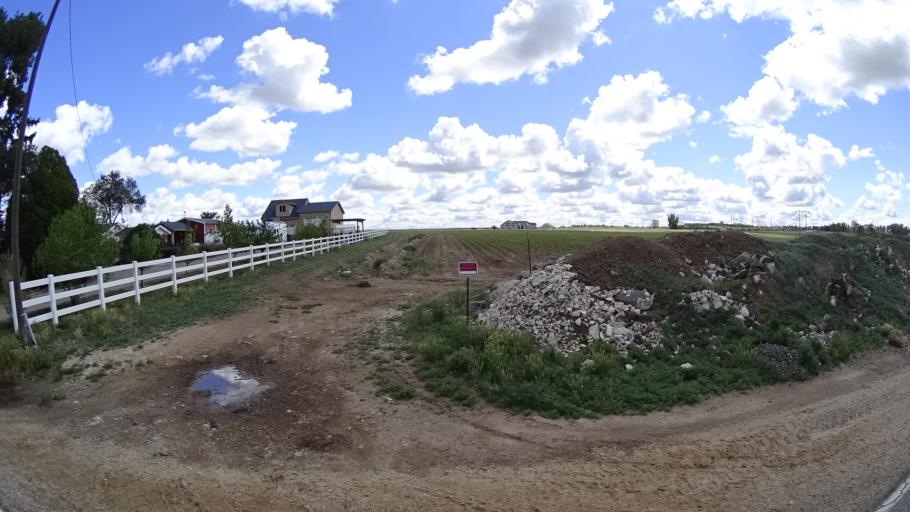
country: US
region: Idaho
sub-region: Ada County
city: Kuna
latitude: 43.5130
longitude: -116.3445
